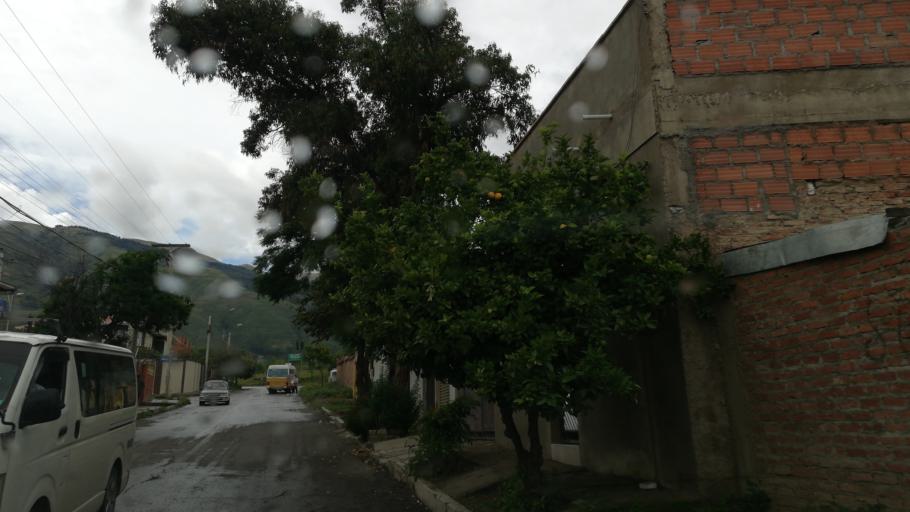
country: BO
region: Cochabamba
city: Cochabamba
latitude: -17.3521
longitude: -66.1759
